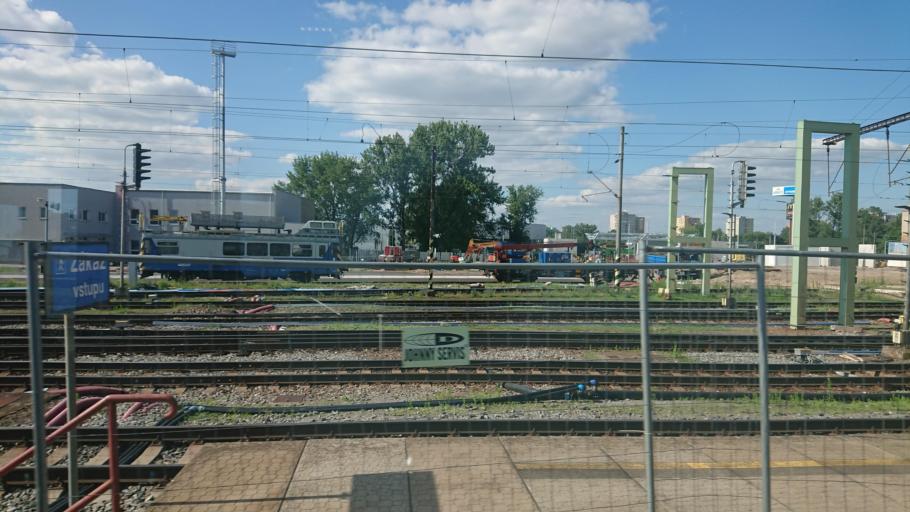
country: CZ
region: Pardubicky
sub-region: Okres Pardubice
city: Pardubice
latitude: 50.0319
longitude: 15.7534
